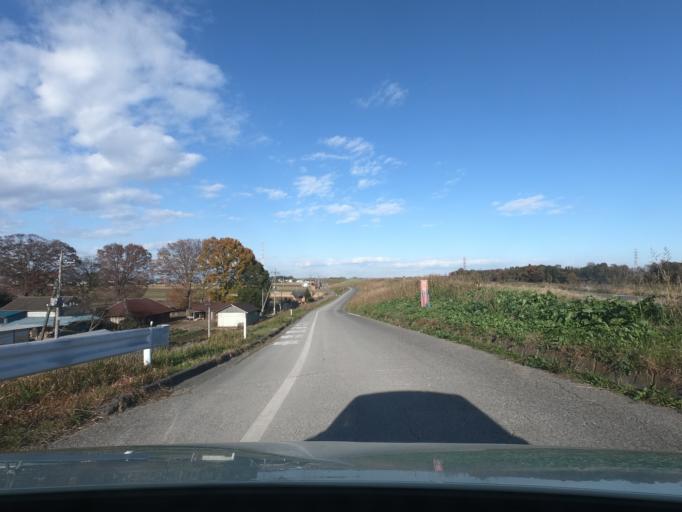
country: JP
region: Ibaraki
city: Koga
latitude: 36.2485
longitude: 139.7337
